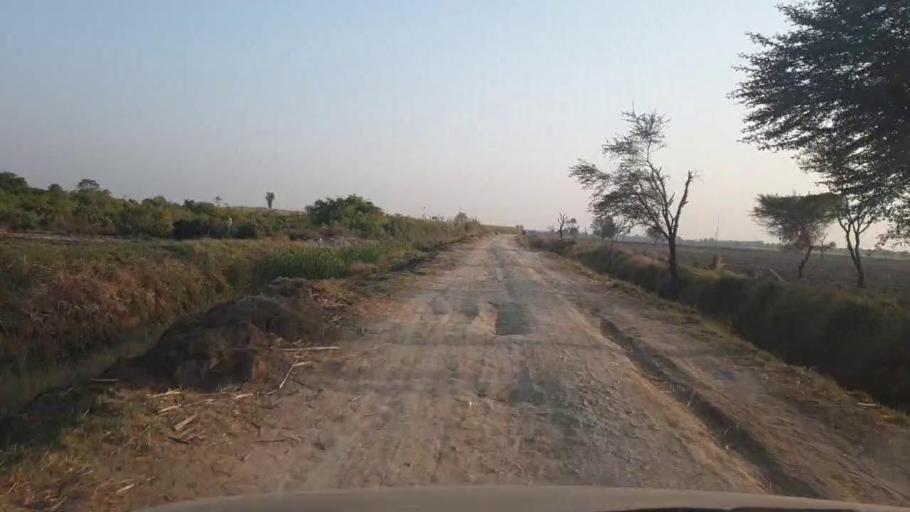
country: PK
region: Sindh
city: Mirwah Gorchani
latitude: 25.3515
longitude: 69.1531
